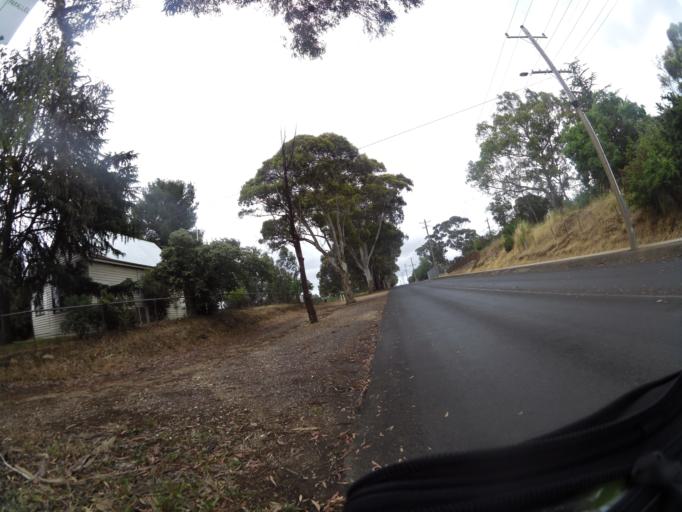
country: AU
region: Victoria
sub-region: Mount Alexander
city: Castlemaine
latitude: -37.0661
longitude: 144.2141
